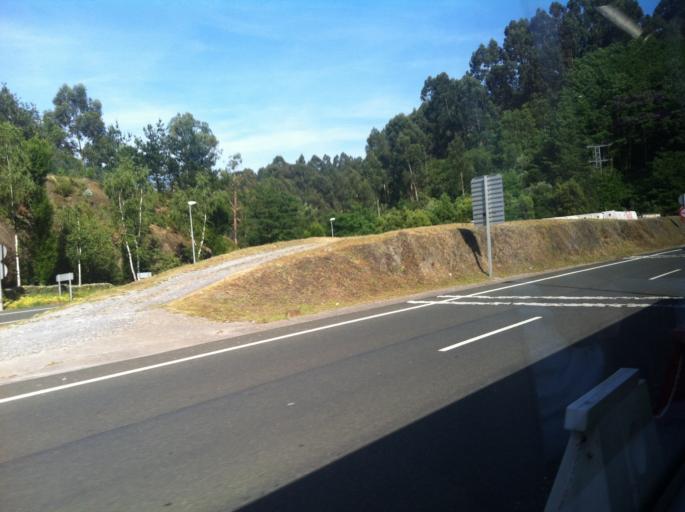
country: ES
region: Basque Country
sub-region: Bizkaia
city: Sondika
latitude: 43.2845
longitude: -2.9346
